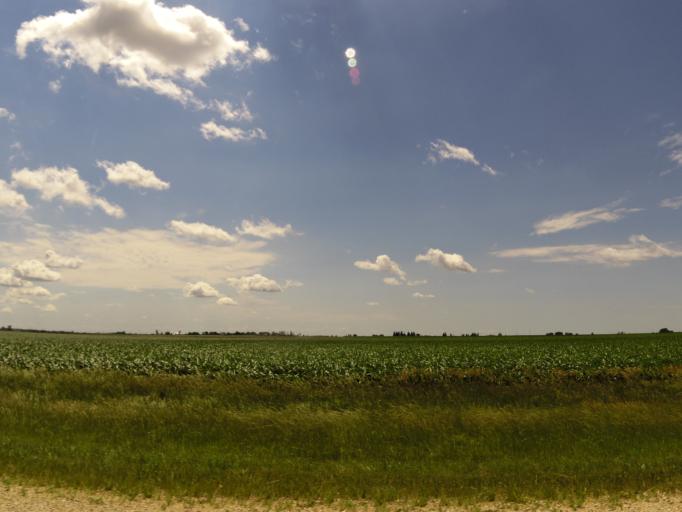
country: US
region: Iowa
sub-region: Fayette County
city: Oelwein
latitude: 42.7149
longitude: -91.9920
